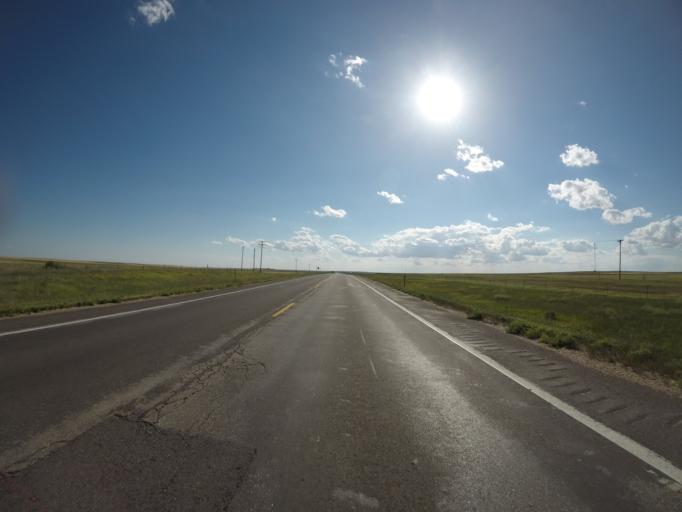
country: US
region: Colorado
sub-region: Morgan County
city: Fort Morgan
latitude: 40.6047
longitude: -103.8498
